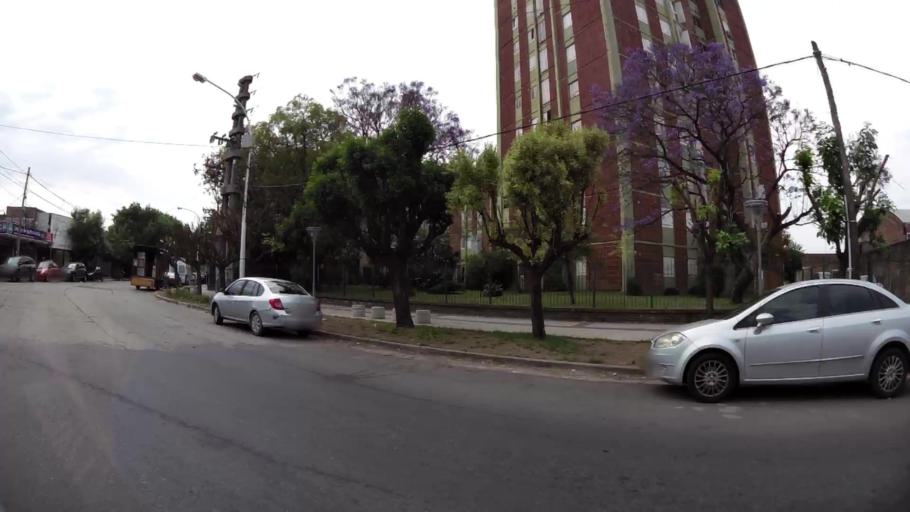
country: AR
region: Buenos Aires F.D.
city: Villa Lugano
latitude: -34.6845
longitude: -58.4917
